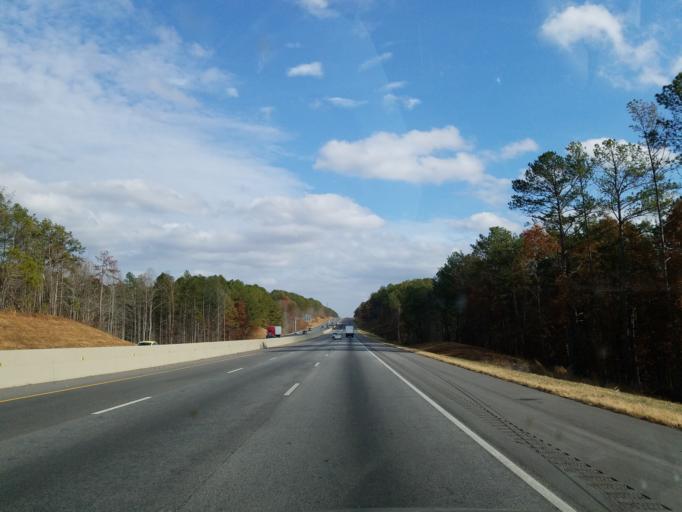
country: US
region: Alabama
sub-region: Cleburne County
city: Heflin
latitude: 33.6474
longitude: -85.4854
